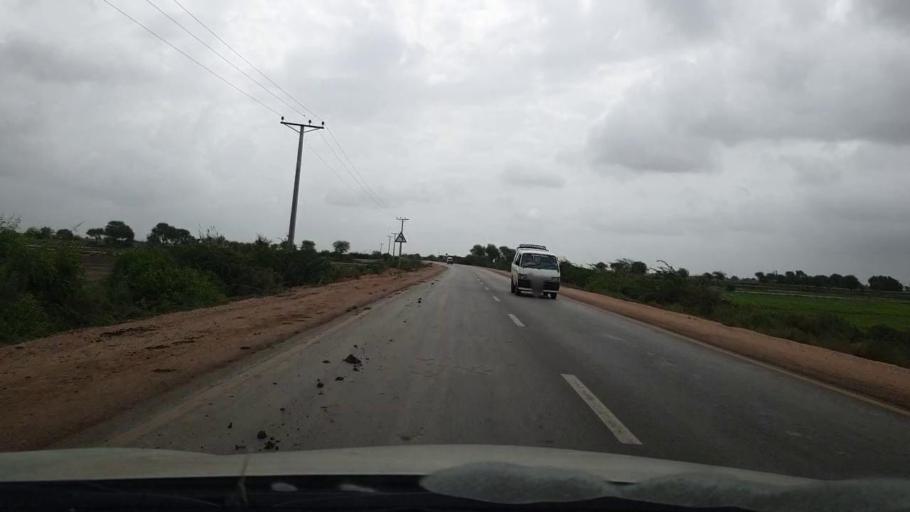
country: PK
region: Sindh
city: Mirpur Batoro
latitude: 24.6212
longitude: 68.3153
